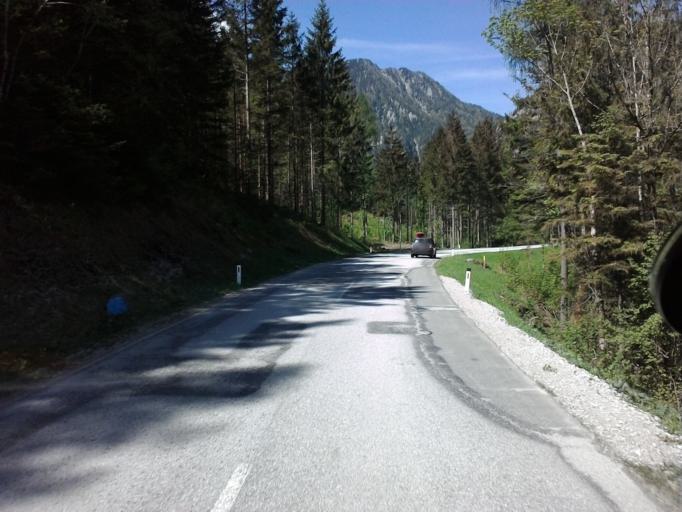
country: AT
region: Styria
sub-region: Politischer Bezirk Liezen
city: Wildalpen
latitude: 47.6882
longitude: 14.9037
